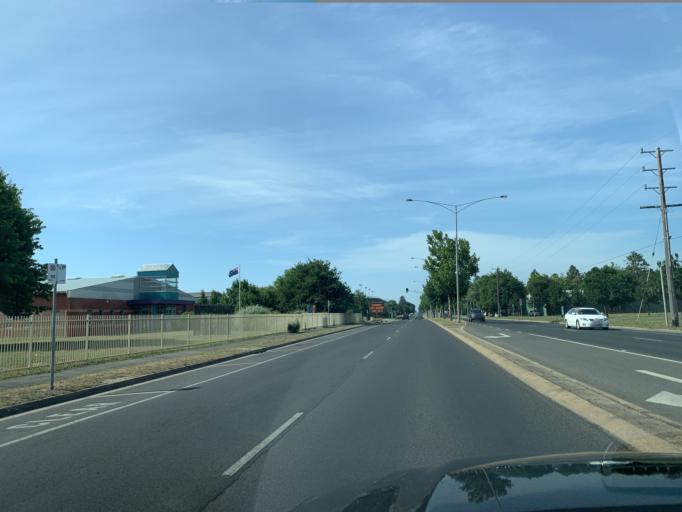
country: AU
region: Victoria
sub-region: Ballarat North
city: Newington
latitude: -37.5530
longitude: 143.8196
